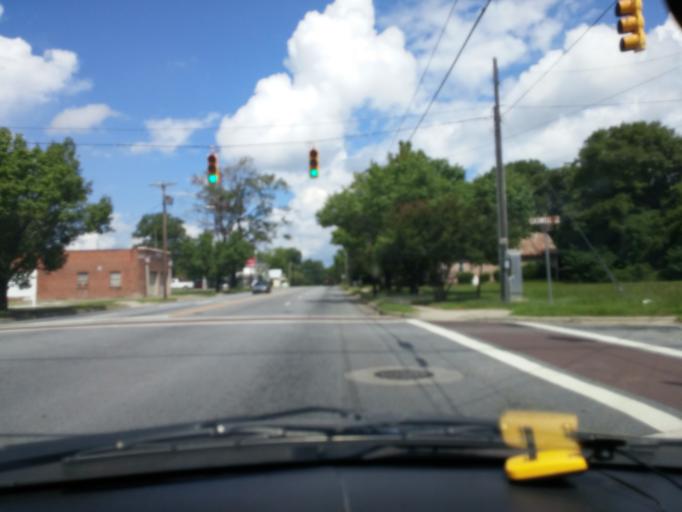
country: US
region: North Carolina
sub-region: Lenoir County
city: Kinston
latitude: 35.2601
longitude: -77.5726
